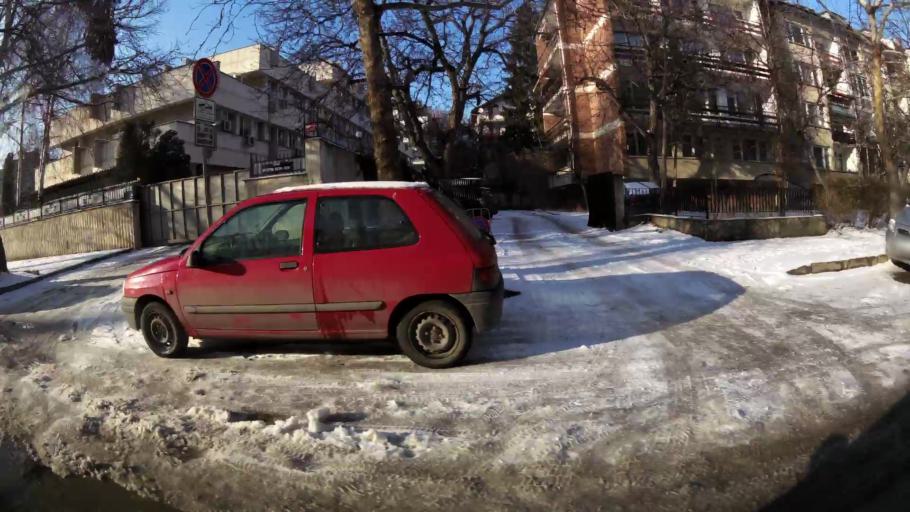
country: BG
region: Sofia-Capital
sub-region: Stolichna Obshtina
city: Sofia
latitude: 42.6704
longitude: 23.3490
